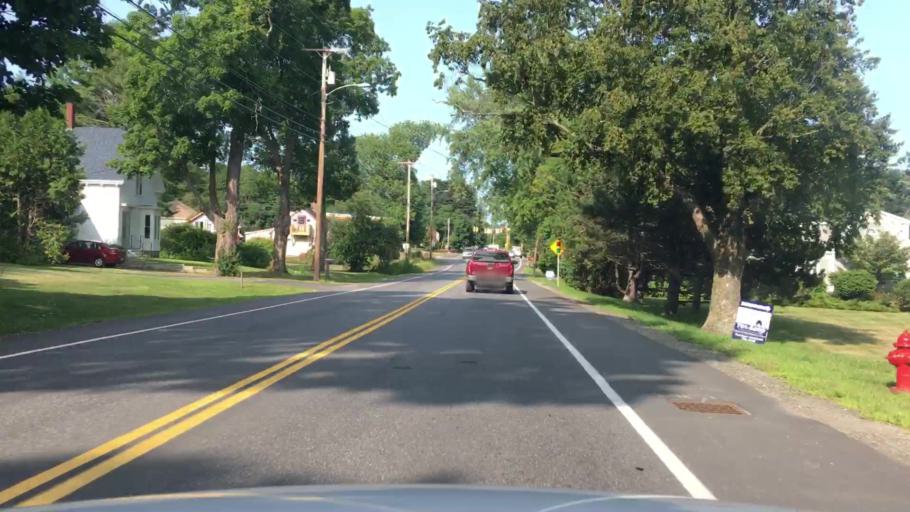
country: US
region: Maine
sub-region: Knox County
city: Rockland
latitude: 44.1224
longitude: -69.1194
